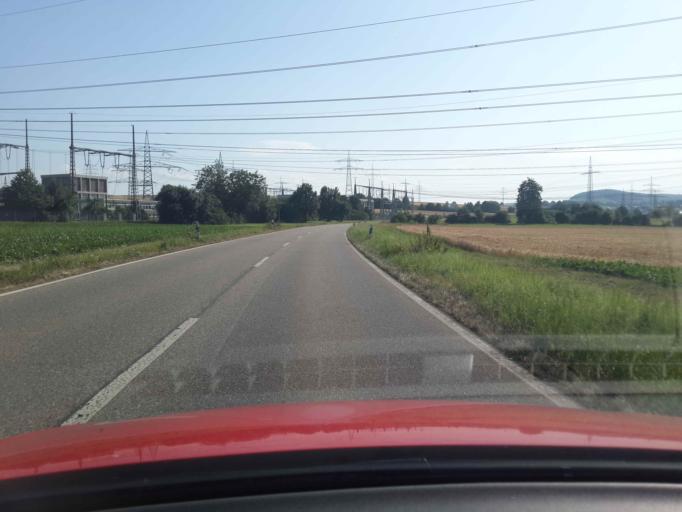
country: DE
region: Baden-Wuerttemberg
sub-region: Regierungsbezirk Stuttgart
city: Leingarten
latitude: 49.1452
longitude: 9.1513
